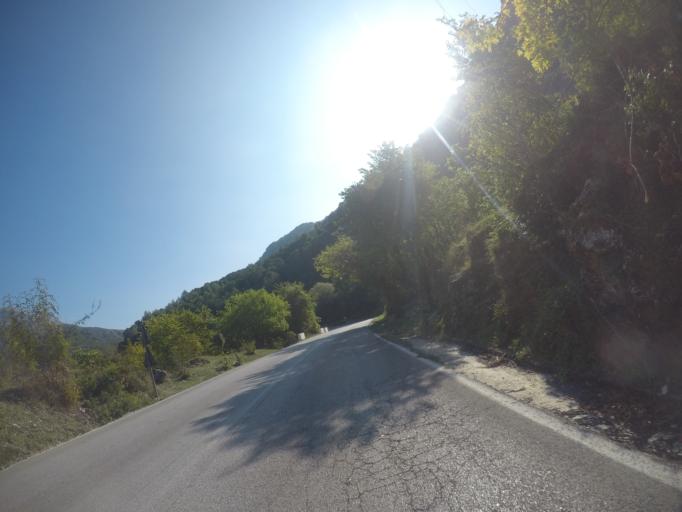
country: AL
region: Vlore
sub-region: Rrethi i Delvines
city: Mesopotam
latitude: 39.9190
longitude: 20.1457
